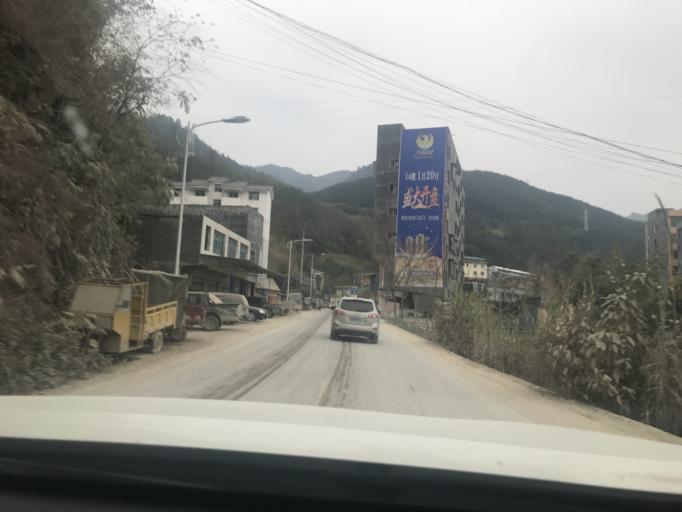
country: CN
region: Guangxi Zhuangzu Zizhiqu
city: Xinzhou
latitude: 24.9833
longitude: 105.8187
